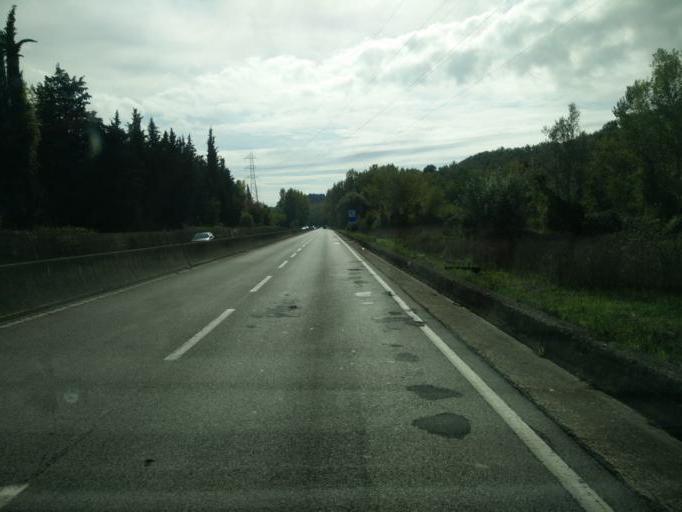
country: IT
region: Tuscany
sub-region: Provincia di Siena
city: Siena
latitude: 43.3223
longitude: 11.2988
